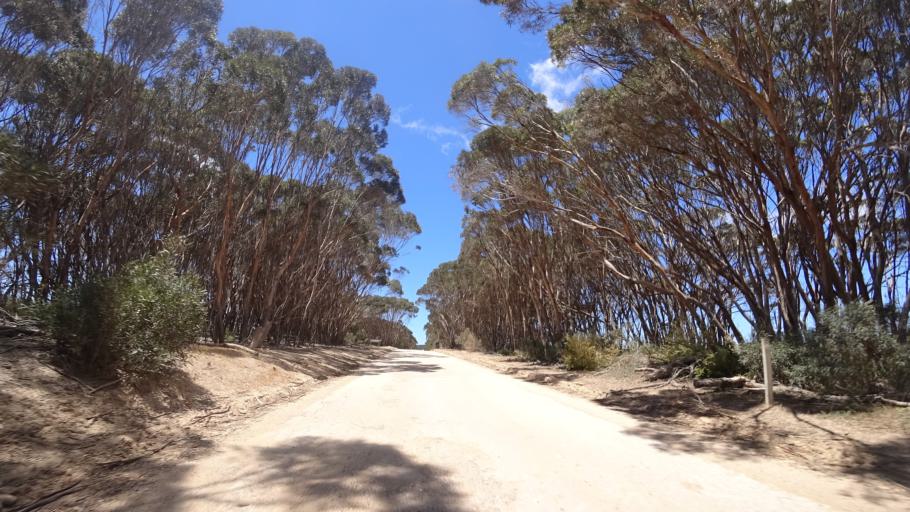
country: AU
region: South Australia
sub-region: Yankalilla
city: Normanville
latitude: -35.8198
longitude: 138.0779
